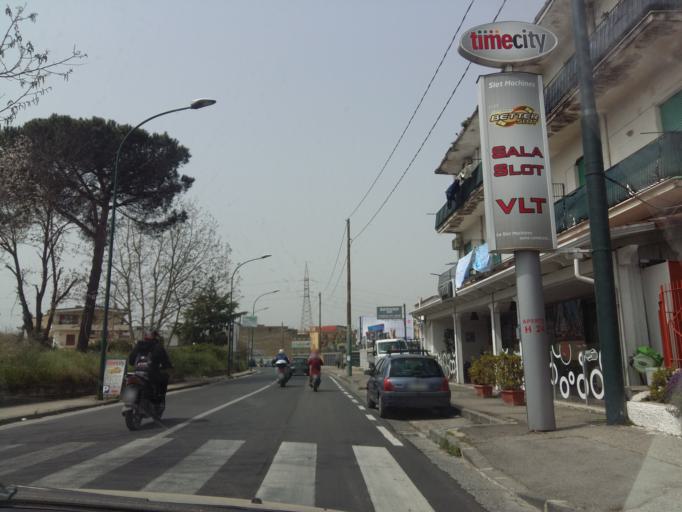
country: IT
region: Campania
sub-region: Provincia di Napoli
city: Mugnano di Napoli
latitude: 40.8973
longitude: 14.2118
